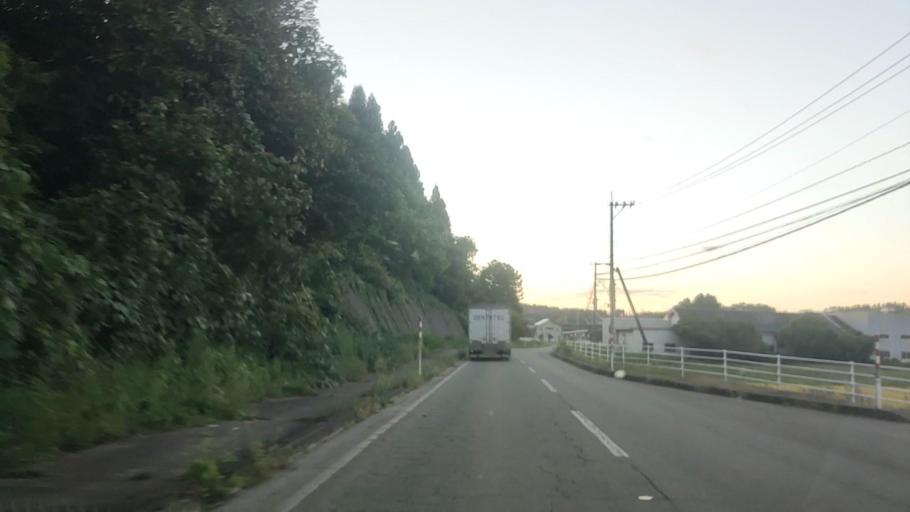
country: JP
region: Ishikawa
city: Tsubata
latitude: 36.6584
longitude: 136.7542
